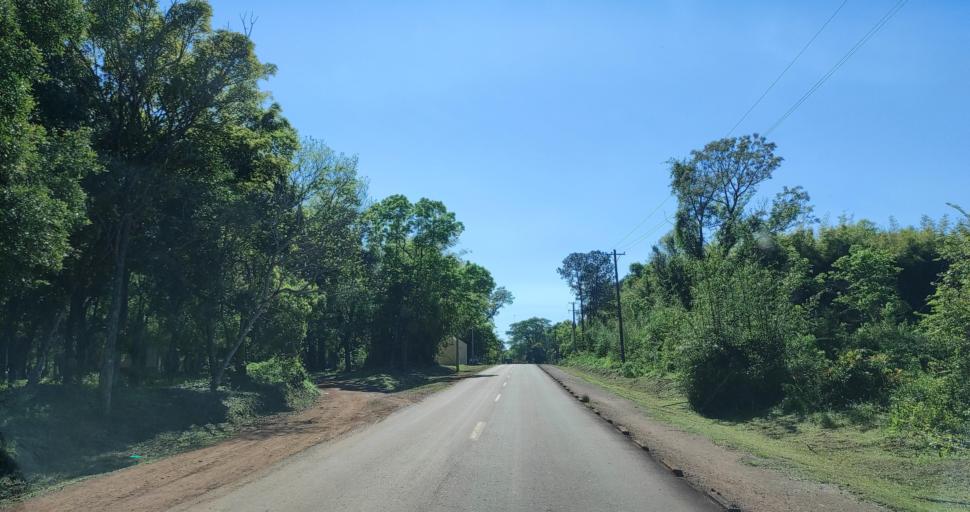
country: AR
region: Misiones
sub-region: Departamento de Candelaria
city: Loreto
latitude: -27.3345
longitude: -55.5238
